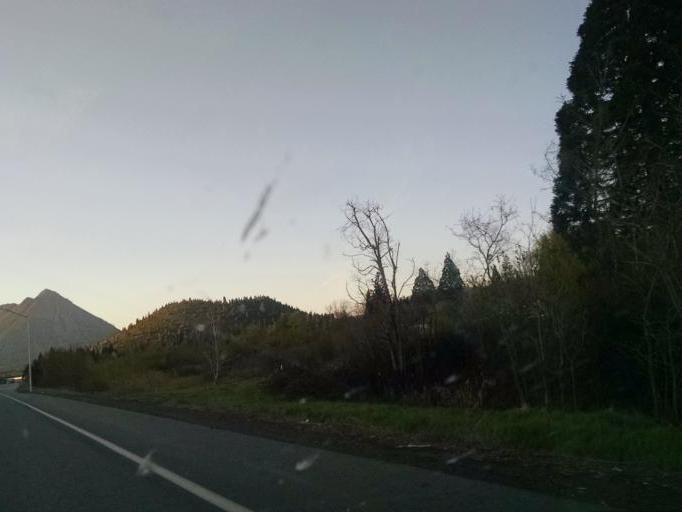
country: US
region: California
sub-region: Siskiyou County
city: Mount Shasta
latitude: 41.3127
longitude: -122.3213
